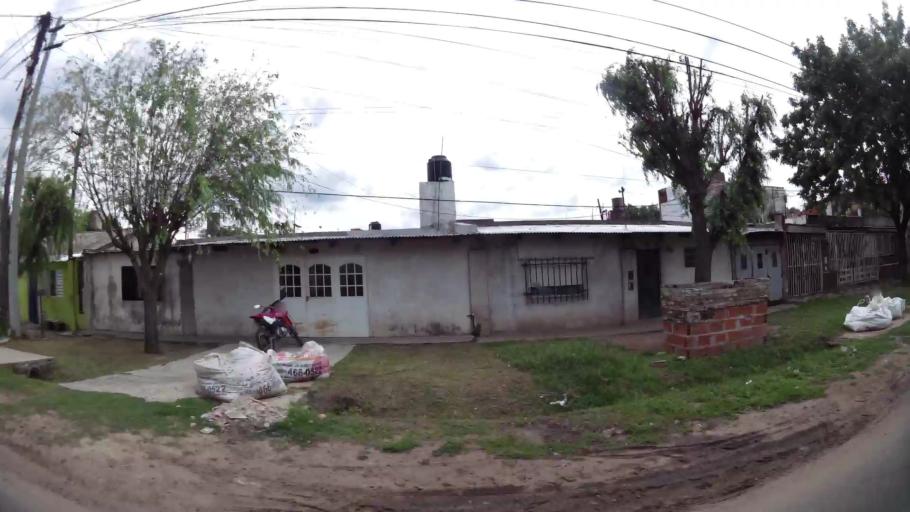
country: AR
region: Santa Fe
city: Gobernador Galvez
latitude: -33.0142
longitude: -60.6542
